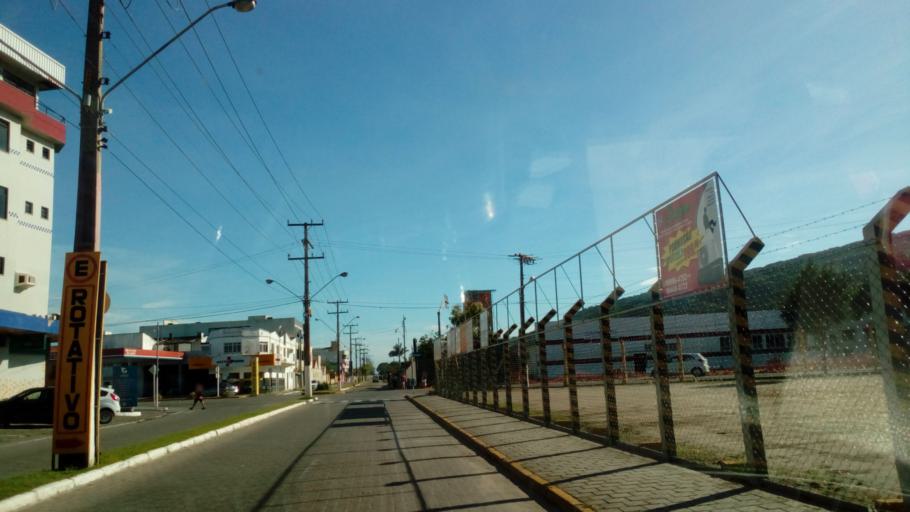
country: BR
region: Santa Catarina
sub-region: Laguna
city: Laguna
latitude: -28.4799
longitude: -48.7843
